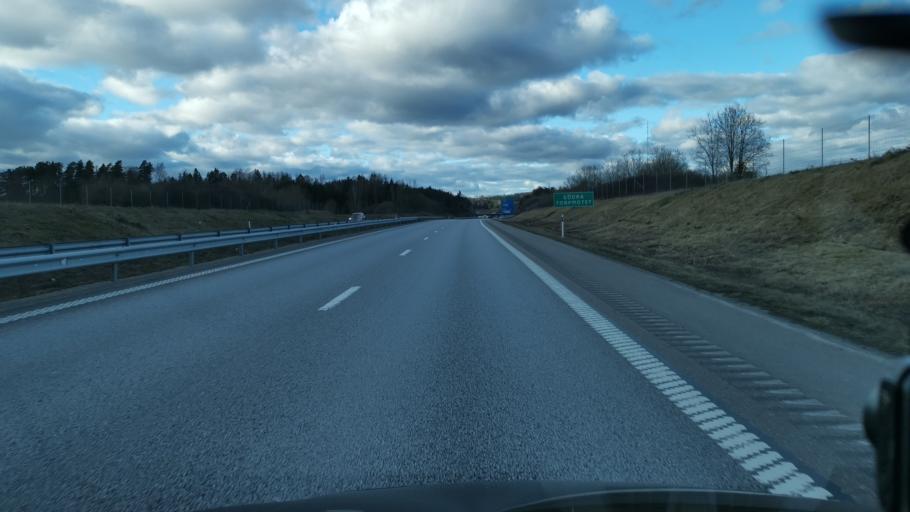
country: SE
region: Vaestra Goetaland
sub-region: Uddevalla Kommun
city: Uddevalla
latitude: 58.3417
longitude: 11.8245
